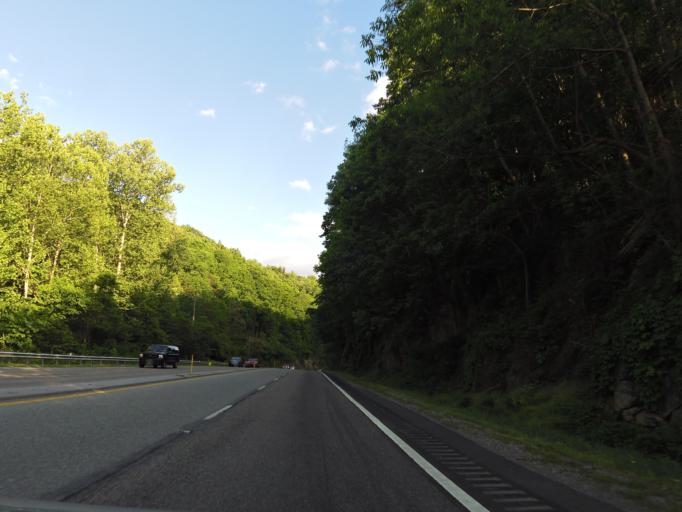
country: US
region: Virginia
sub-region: Washington County
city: Abingdon
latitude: 36.7577
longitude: -82.0596
